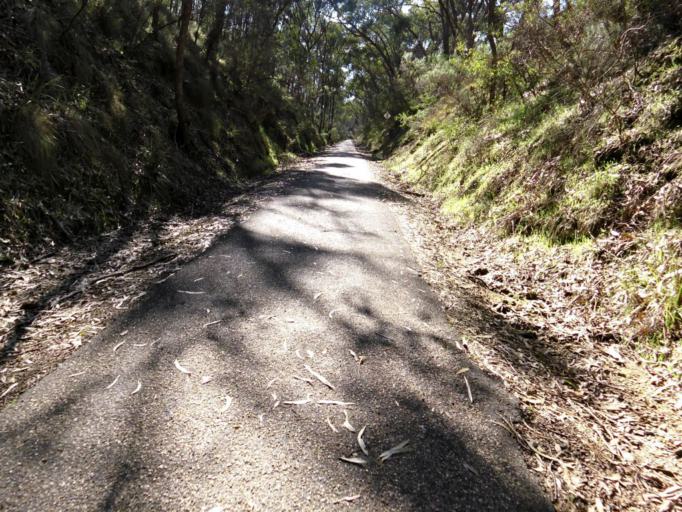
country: AU
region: Victoria
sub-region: Wangaratta
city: Wangaratta
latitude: -36.4096
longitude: 146.6150
